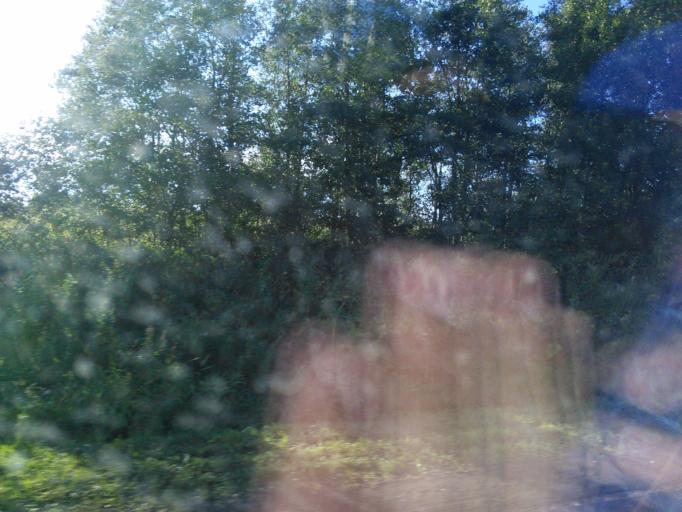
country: RU
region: Jaroslavl
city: Poshekhon'ye
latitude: 58.4598
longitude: 39.0410
